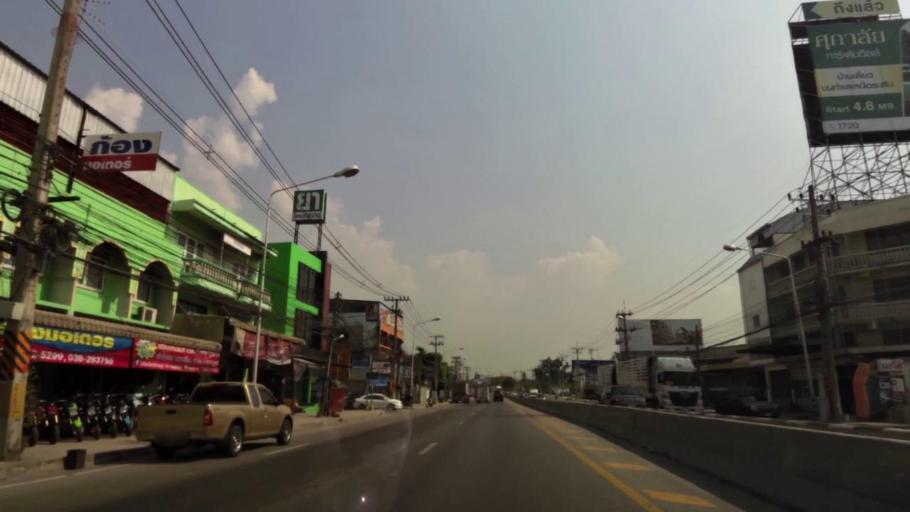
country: TH
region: Chon Buri
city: Chon Buri
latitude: 13.3506
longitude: 101.0102
